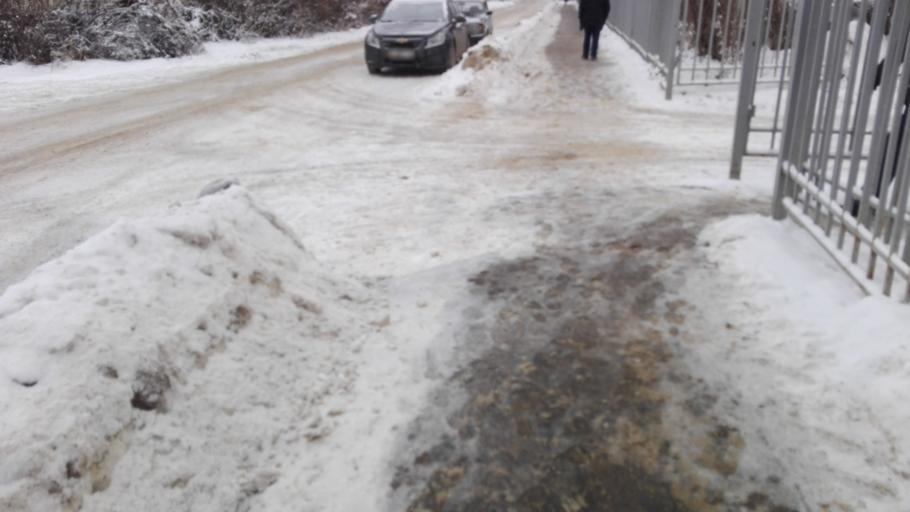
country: RU
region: Tula
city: Kosaya Gora
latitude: 54.1177
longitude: 37.5347
